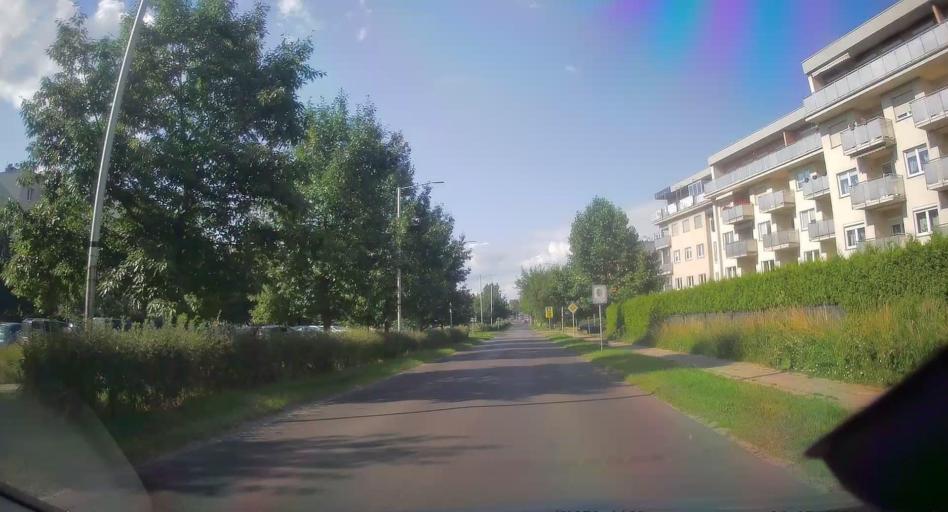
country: PL
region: Silesian Voivodeship
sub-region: Czestochowa
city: Czestochowa
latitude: 50.8204
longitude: 19.0994
